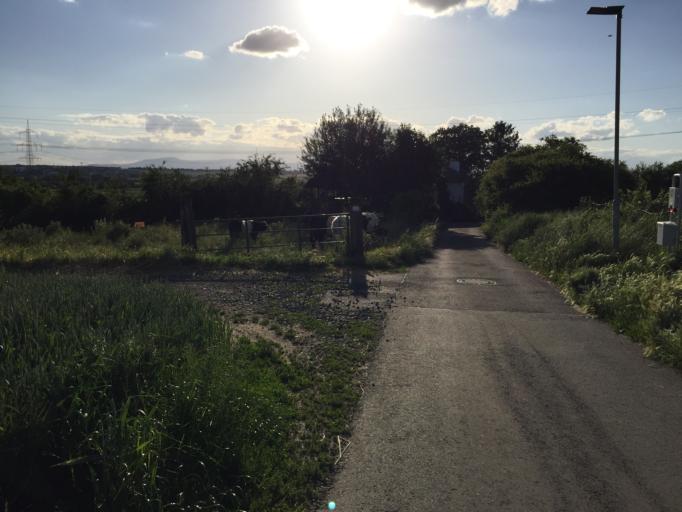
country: DE
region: Hesse
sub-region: Regierungsbezirk Darmstadt
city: Karben
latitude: 50.2139
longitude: 8.7835
